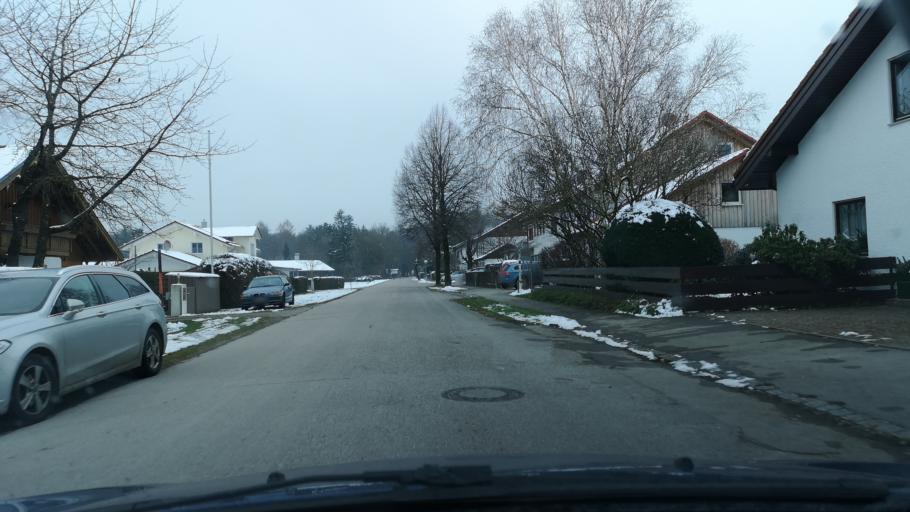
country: DE
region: Bavaria
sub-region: Upper Bavaria
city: Anzing
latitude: 48.1433
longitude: 11.8632
